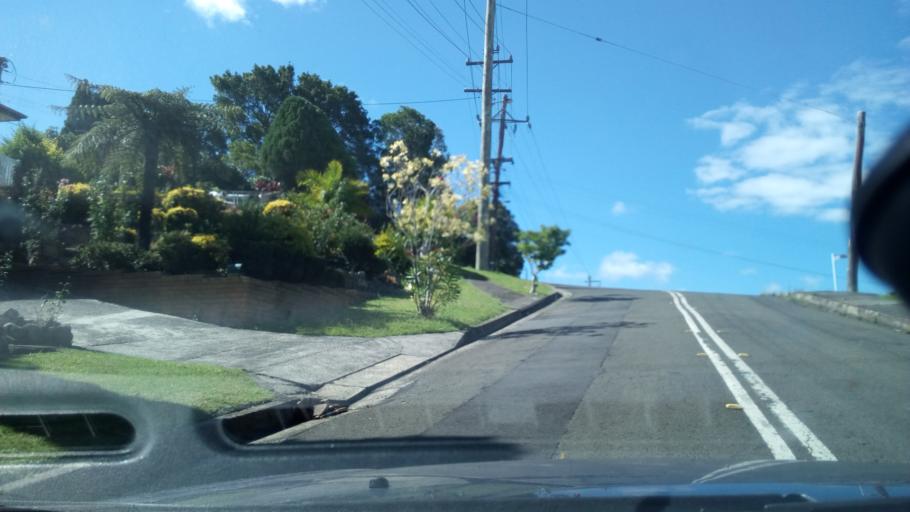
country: AU
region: New South Wales
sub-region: Wollongong
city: Mount Ousley
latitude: -34.3946
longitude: 150.8701
